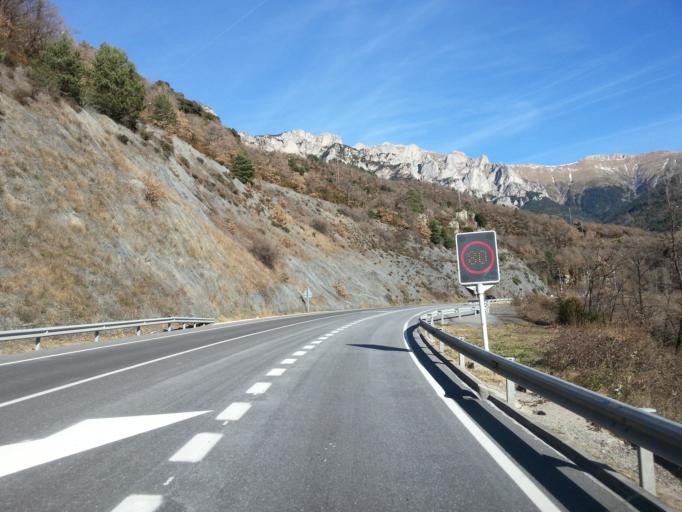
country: ES
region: Catalonia
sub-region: Provincia de Barcelona
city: Baga
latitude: 42.2926
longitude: 1.8591
